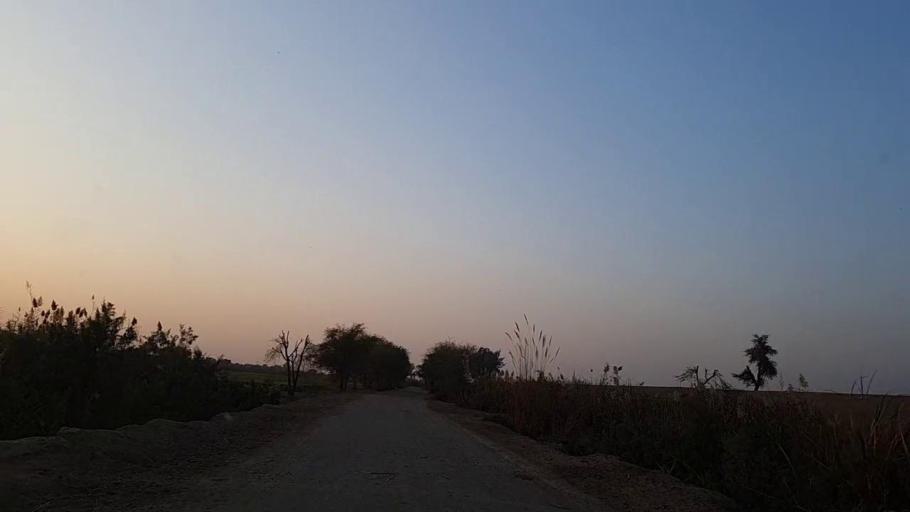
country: PK
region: Sindh
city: Bhit Shah
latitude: 25.9191
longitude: 68.4965
